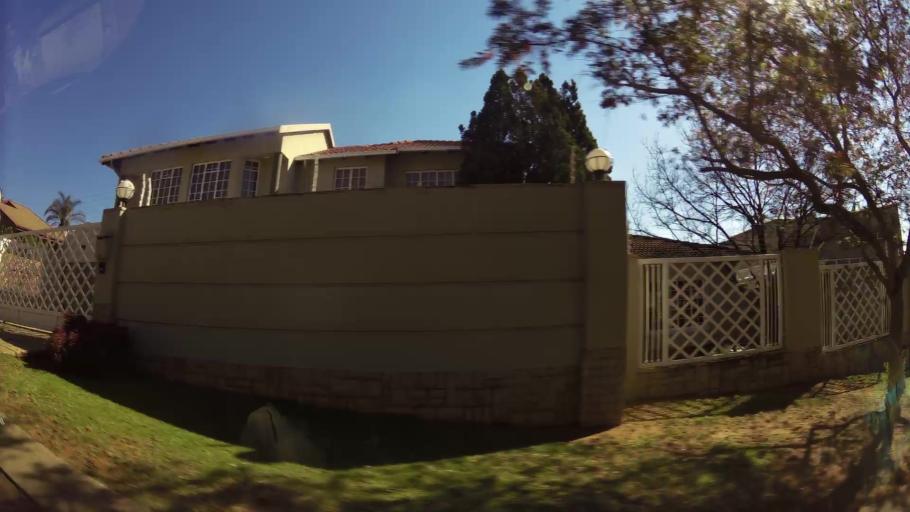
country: ZA
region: Gauteng
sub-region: City of Tshwane Metropolitan Municipality
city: Centurion
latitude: -25.8559
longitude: 28.1758
